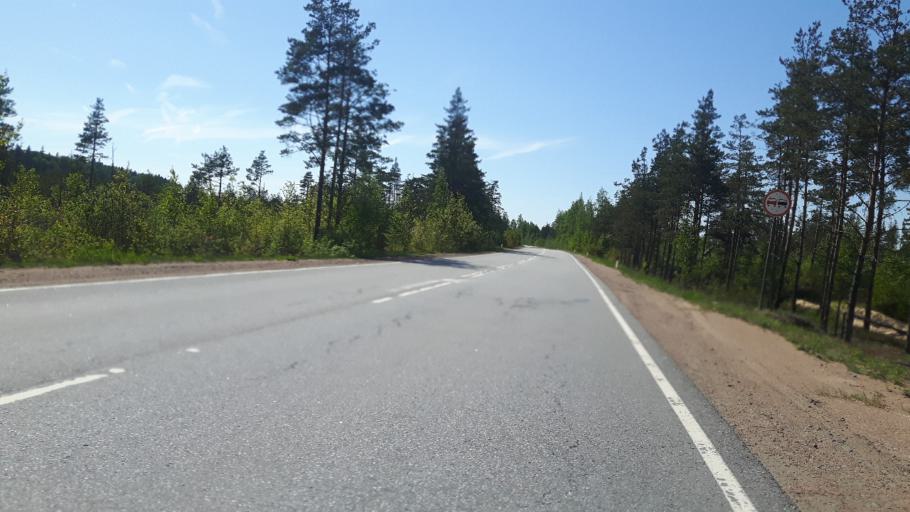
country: RU
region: Leningrad
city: Sista-Palkino
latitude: 59.7696
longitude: 28.7839
